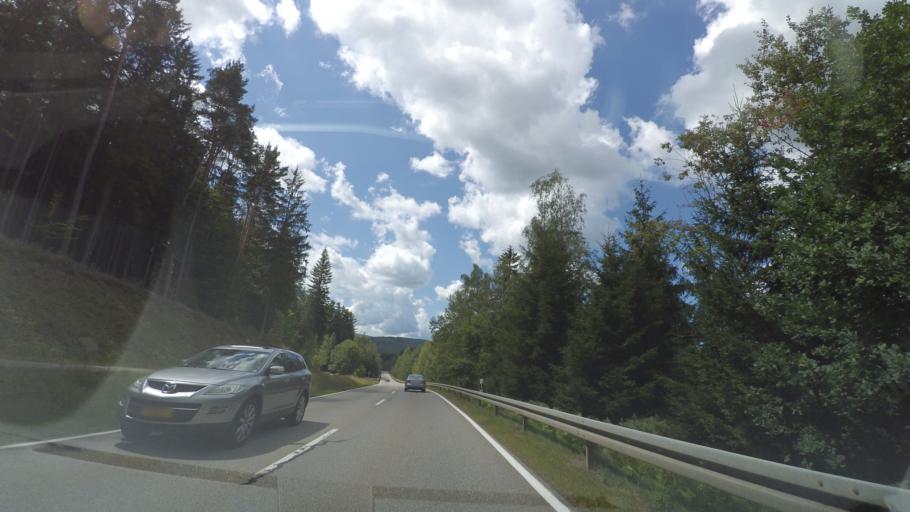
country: DE
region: Bavaria
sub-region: Lower Bavaria
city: Teisnach
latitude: 49.0466
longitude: 13.0105
